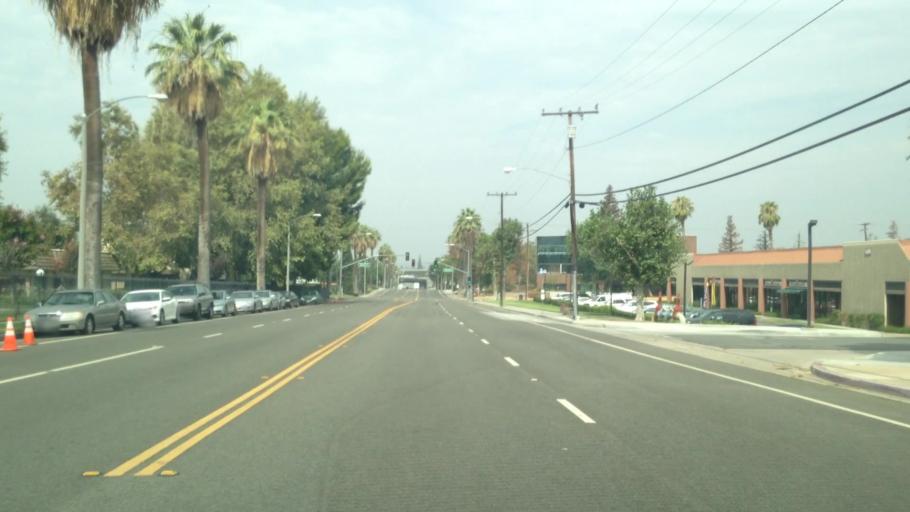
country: US
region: California
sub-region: Riverside County
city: Highgrove
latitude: 33.9903
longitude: -117.3423
